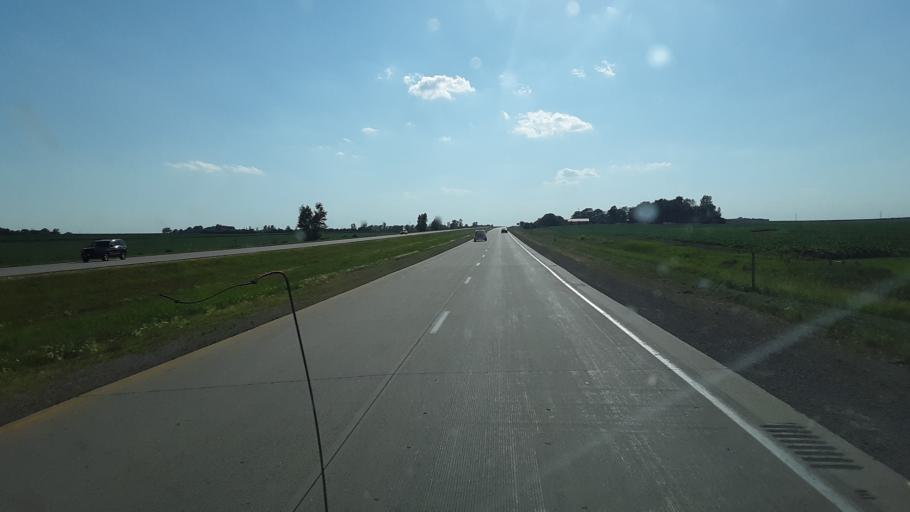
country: US
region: Iowa
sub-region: Grundy County
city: Dike
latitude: 42.4634
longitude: -92.7228
